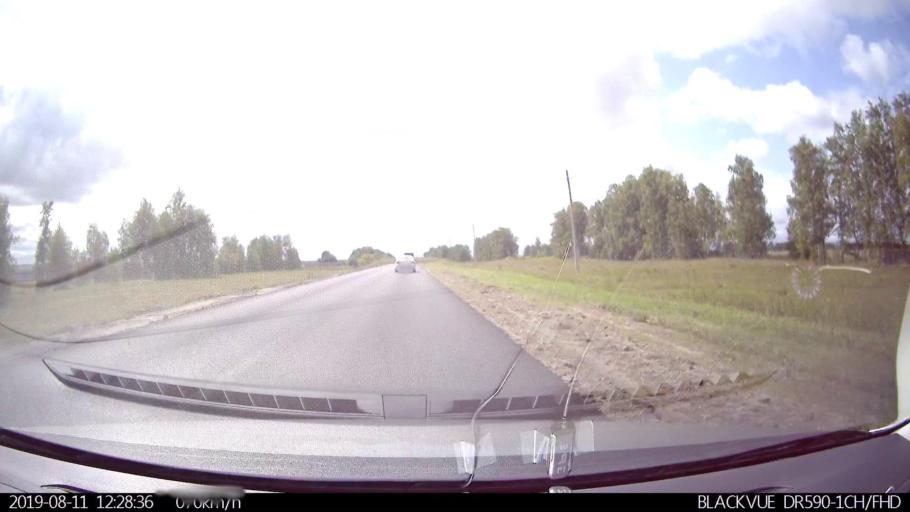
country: RU
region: Ulyanovsk
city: Ignatovka
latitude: 53.8425
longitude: 47.9104
